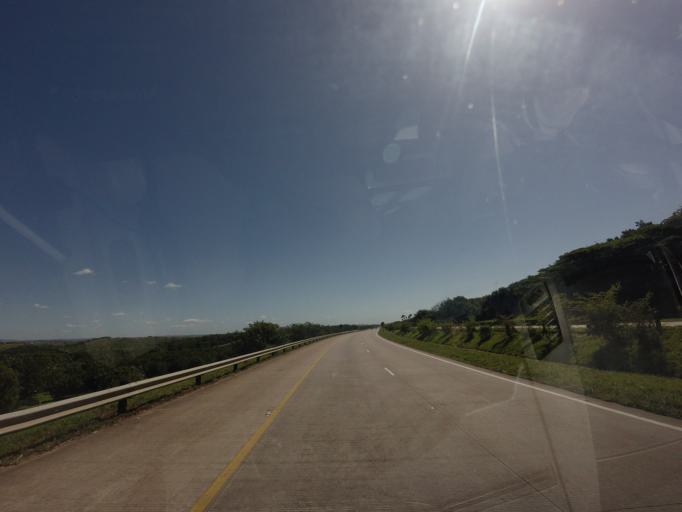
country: ZA
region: KwaZulu-Natal
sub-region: iLembe District Municipality
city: Ballitoville
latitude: -29.4722
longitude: 31.2334
